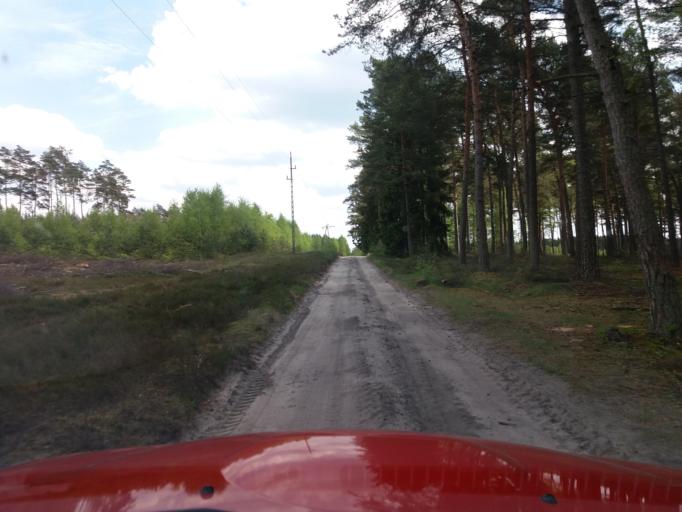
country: PL
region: West Pomeranian Voivodeship
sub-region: Powiat choszczenski
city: Drawno
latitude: 53.1392
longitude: 15.7312
